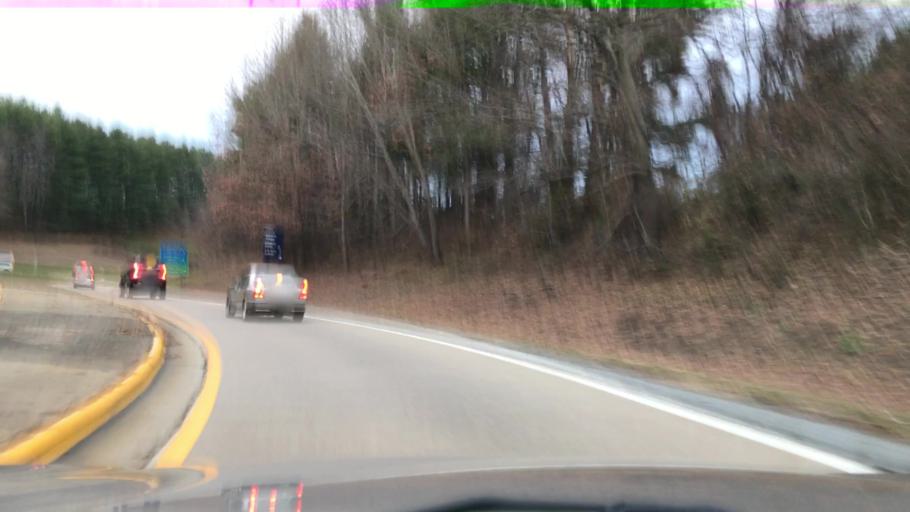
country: US
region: North Carolina
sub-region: Buncombe County
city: Biltmore Forest
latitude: 35.5597
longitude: -82.5377
